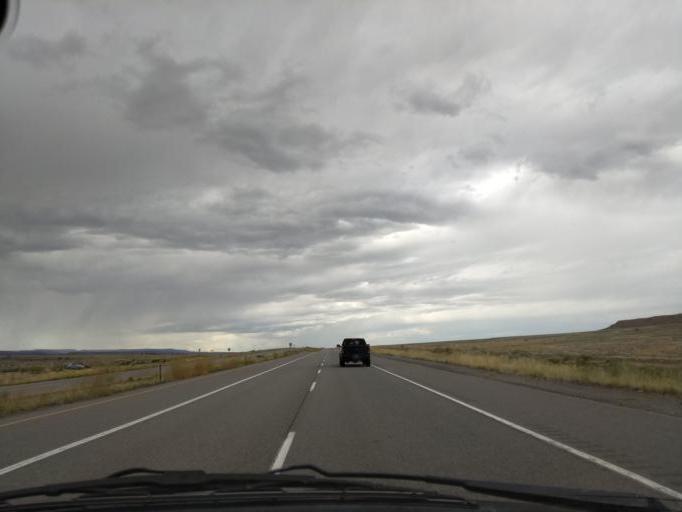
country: US
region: Colorado
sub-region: Delta County
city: Delta
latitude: 38.7837
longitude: -108.2449
